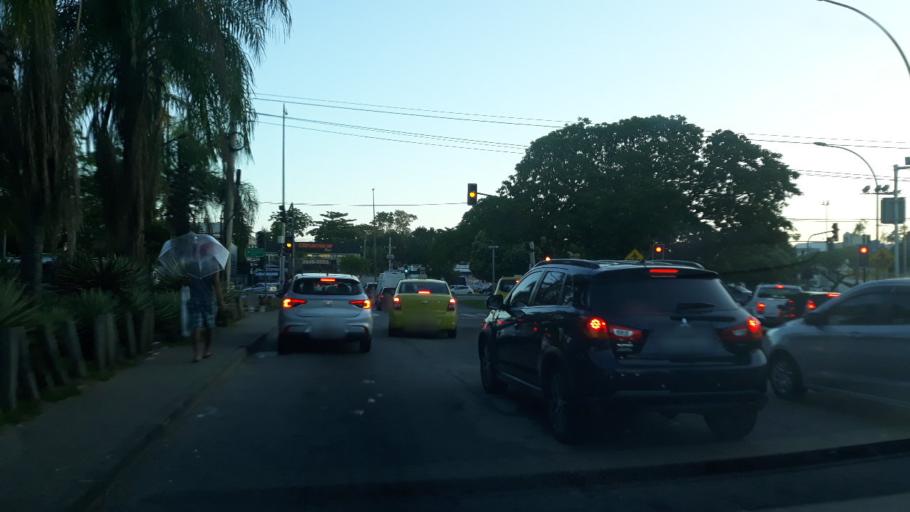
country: BR
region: Rio de Janeiro
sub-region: Rio De Janeiro
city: Rio de Janeiro
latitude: -22.9993
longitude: -43.3547
